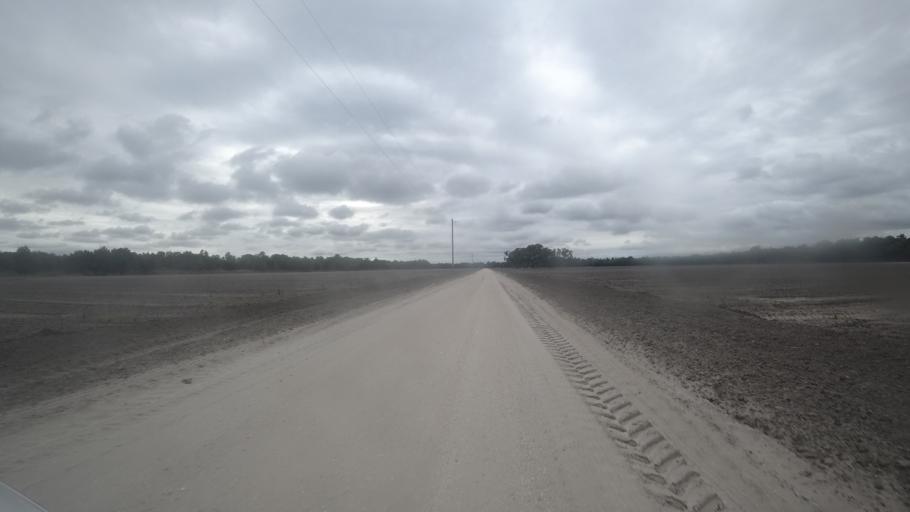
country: US
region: Florida
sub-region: Hillsborough County
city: Wimauma
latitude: 27.5813
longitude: -82.1263
